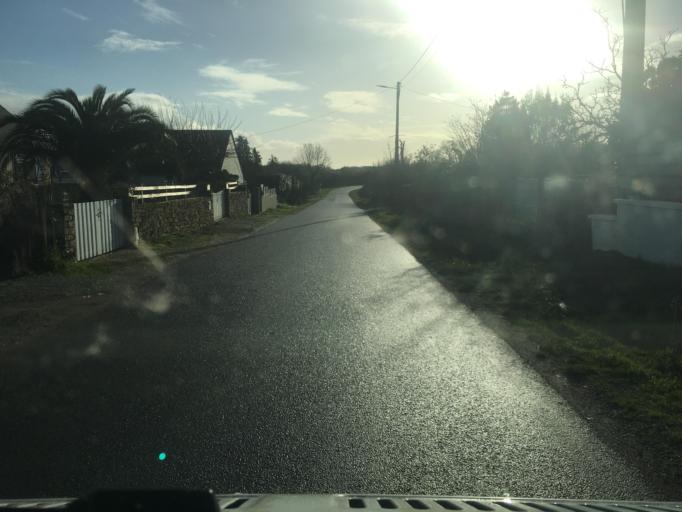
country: FR
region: Brittany
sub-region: Departement du Morbihan
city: Surzur
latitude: 47.5159
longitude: -2.6731
